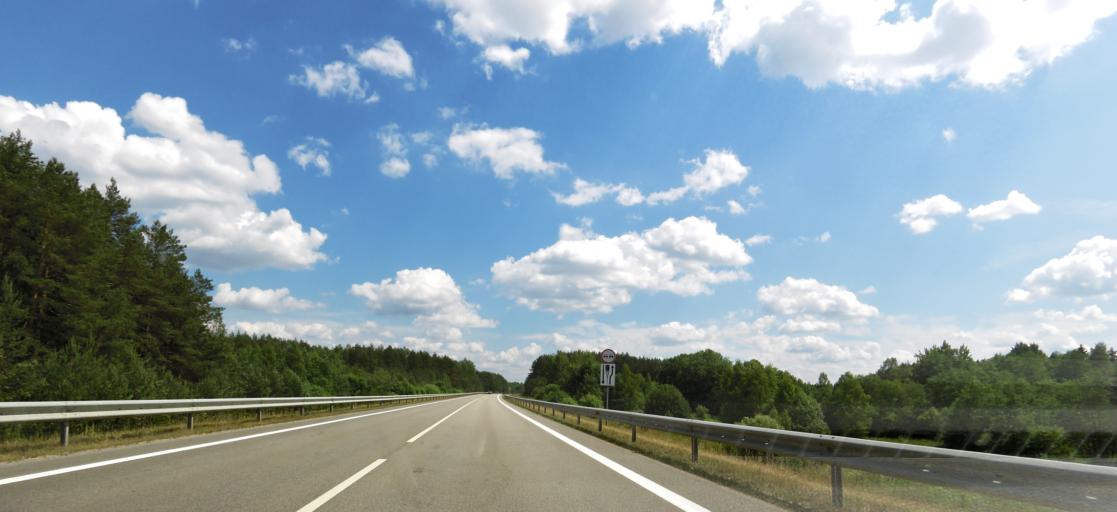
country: LT
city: Skaidiskes
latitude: 54.5929
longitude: 25.5497
